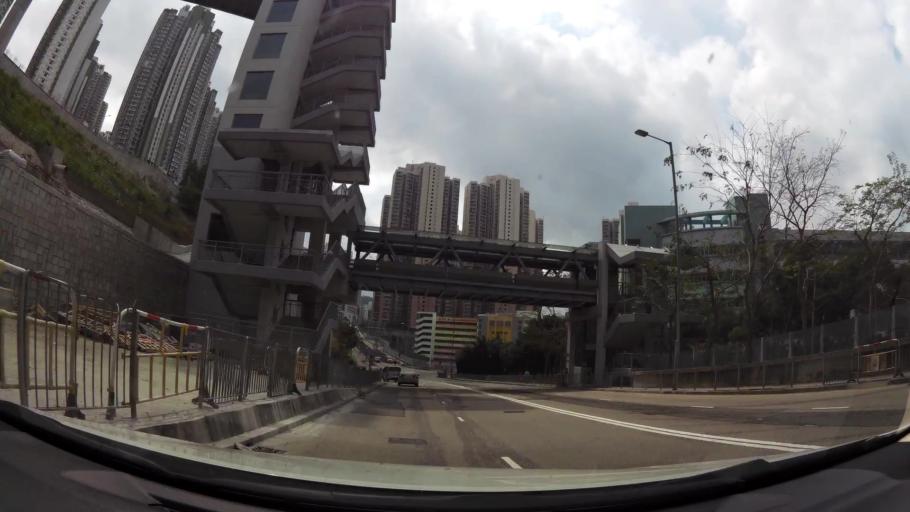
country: HK
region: Kowloon City
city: Kowloon
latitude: 22.3214
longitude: 114.2320
